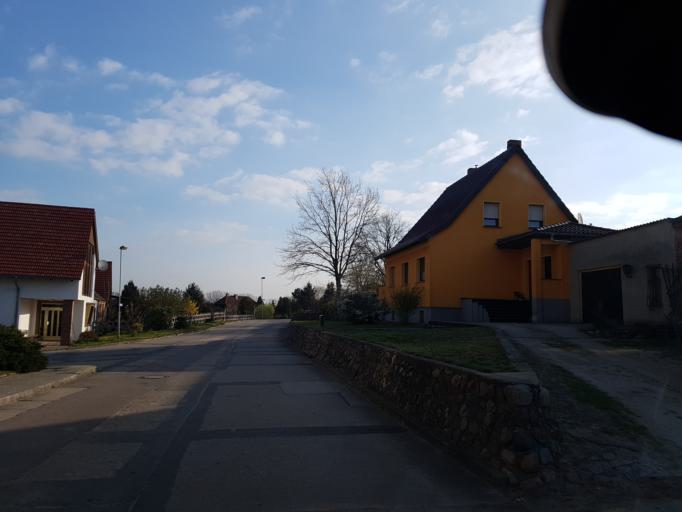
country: DE
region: Brandenburg
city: Treuenbrietzen
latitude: 52.1151
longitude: 12.8247
